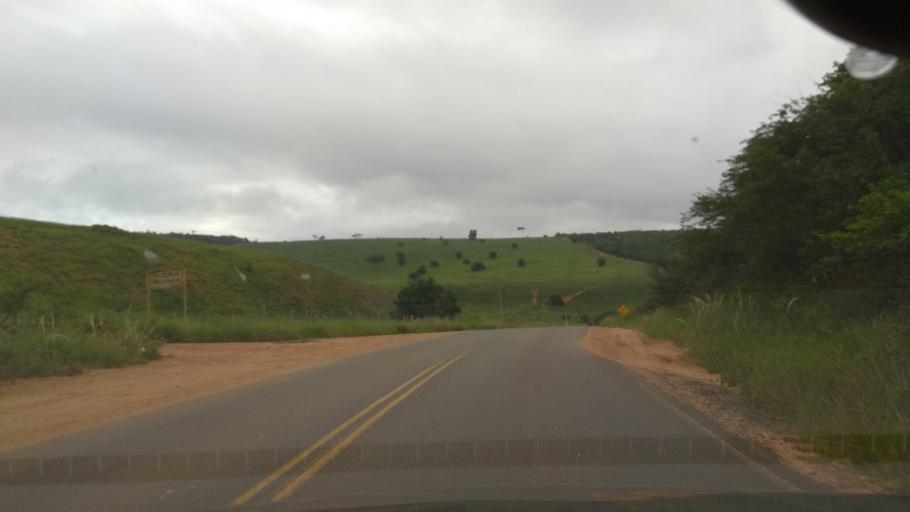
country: BR
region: Bahia
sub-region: Santa Ines
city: Santa Ines
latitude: -13.2550
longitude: -39.7836
